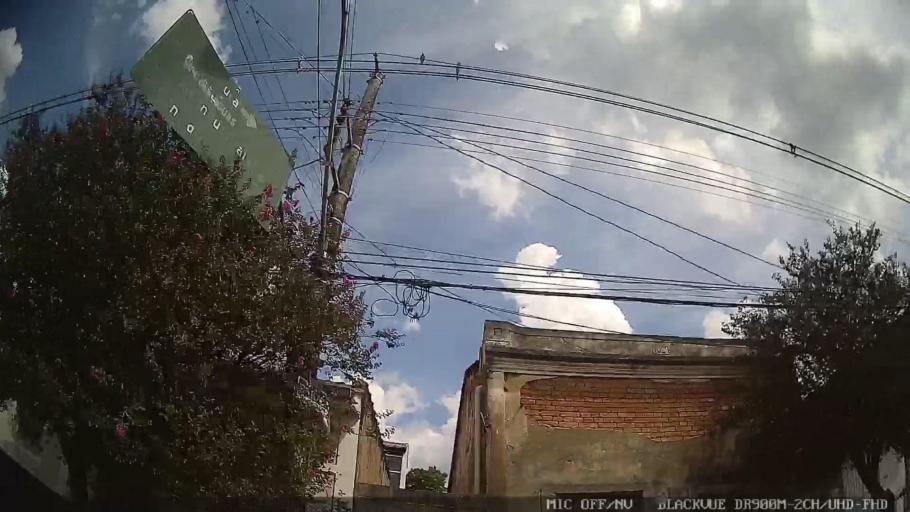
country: BR
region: Sao Paulo
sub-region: Braganca Paulista
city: Braganca Paulista
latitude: -22.9688
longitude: -46.5461
